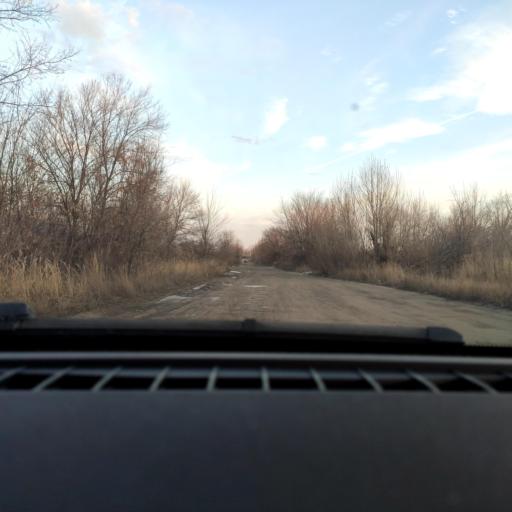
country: RU
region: Voronezj
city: Maslovka
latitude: 51.6084
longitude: 39.2664
